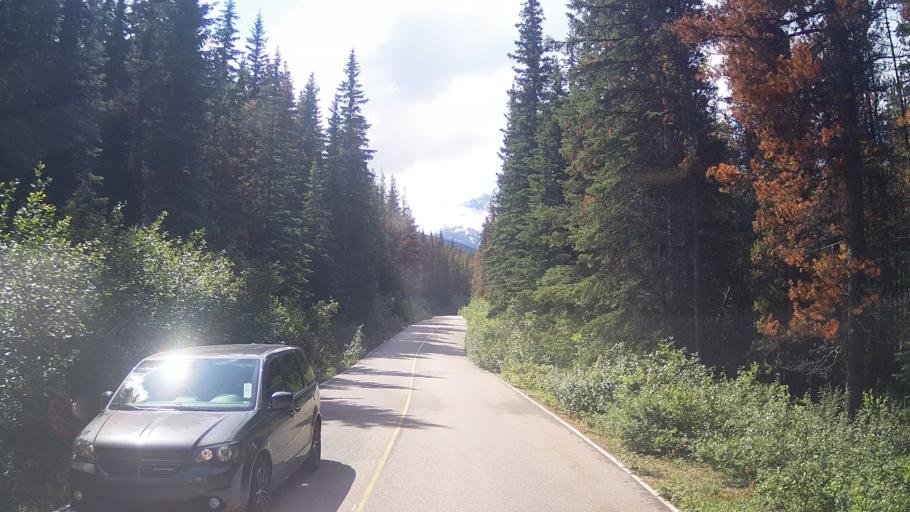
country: CA
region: Alberta
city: Jasper Park Lodge
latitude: 52.7491
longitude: -118.0468
